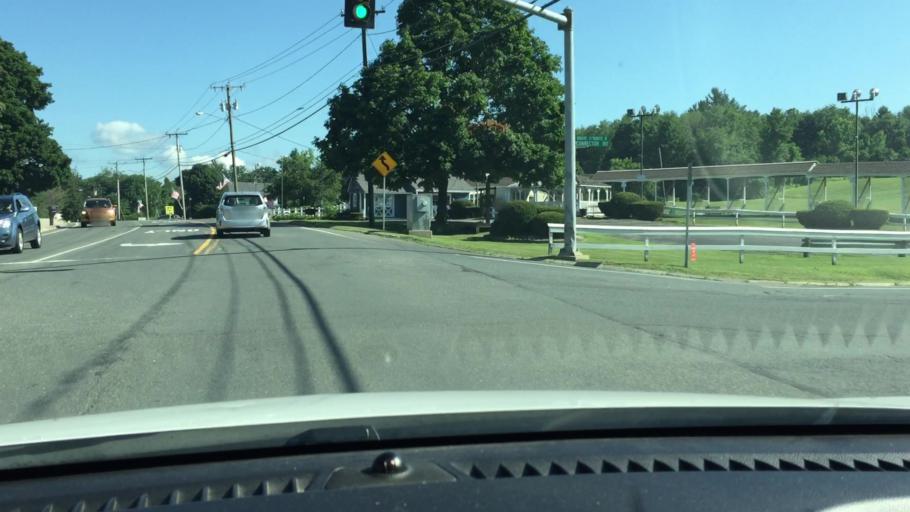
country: US
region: Massachusetts
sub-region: Berkshire County
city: Lanesborough
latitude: 42.4963
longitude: -73.2374
